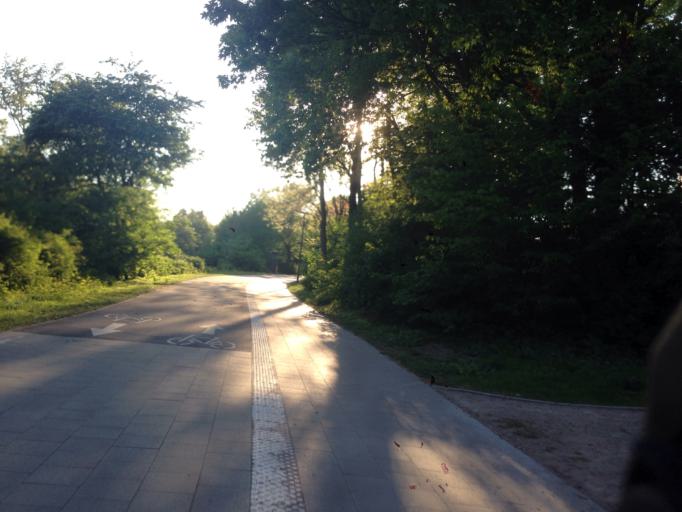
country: DE
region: Hamburg
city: Borgfelde
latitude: 53.5555
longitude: 10.0574
